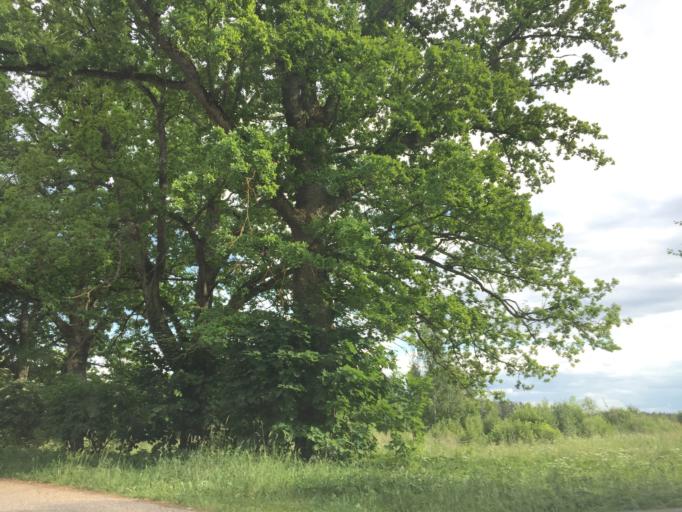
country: LV
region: Pargaujas
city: Stalbe
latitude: 57.3460
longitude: 24.9475
